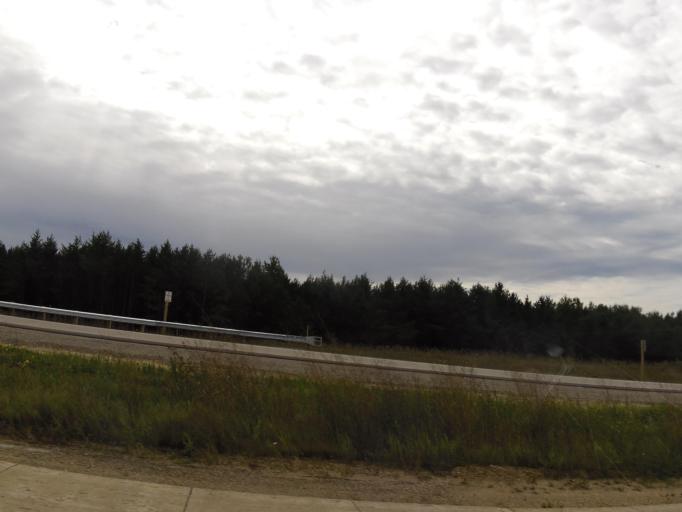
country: US
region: Wisconsin
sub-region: Monroe County
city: Sparta
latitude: 43.9103
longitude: -90.8720
